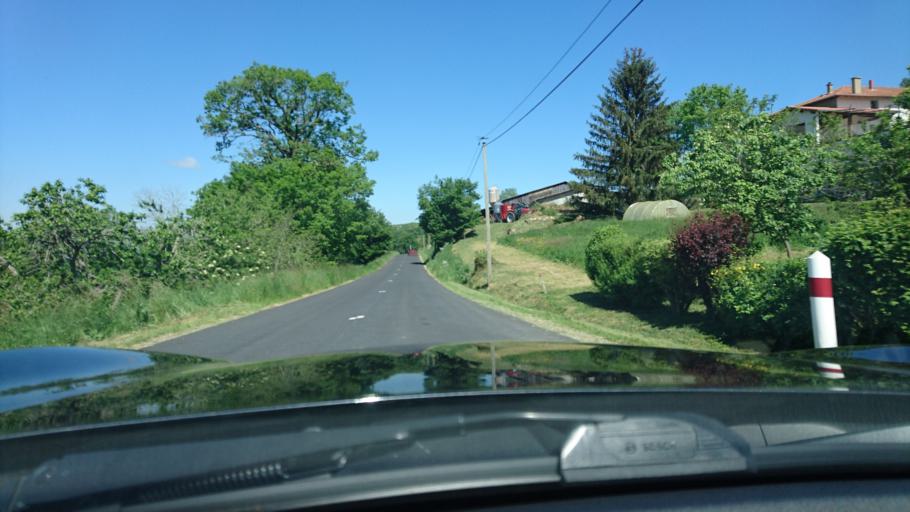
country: FR
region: Rhone-Alpes
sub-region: Departement de la Loire
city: Violay
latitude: 45.8626
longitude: 4.3569
